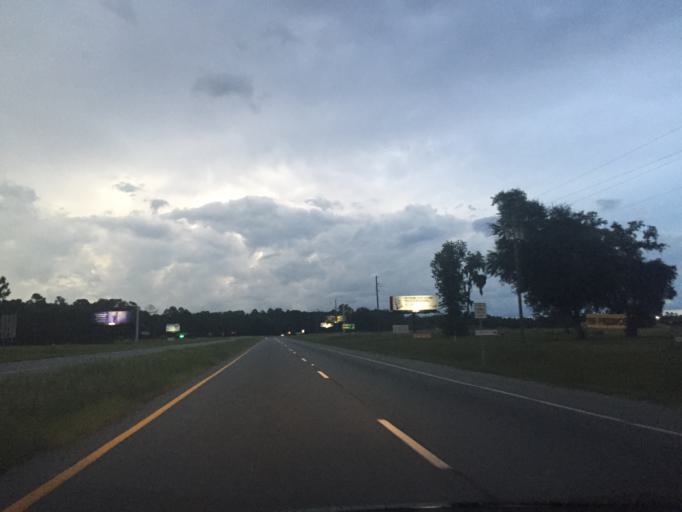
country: US
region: Georgia
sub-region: Liberty County
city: Hinesville
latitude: 31.8228
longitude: -81.5200
